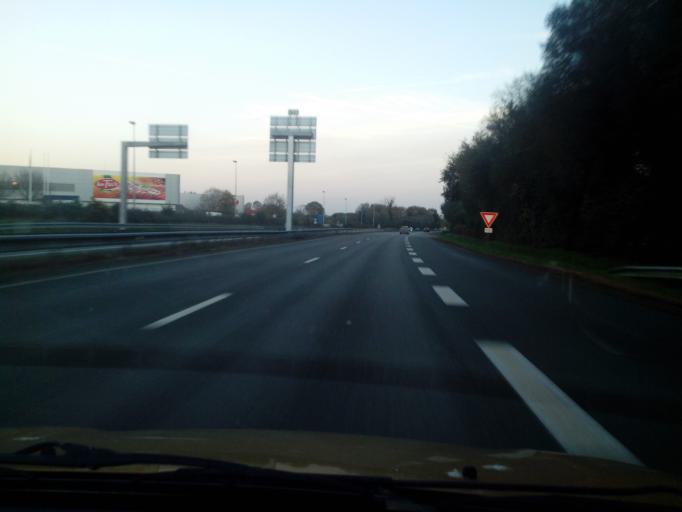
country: FR
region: Brittany
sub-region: Departement du Morbihan
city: Baud
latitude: 47.8951
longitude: -3.0103
